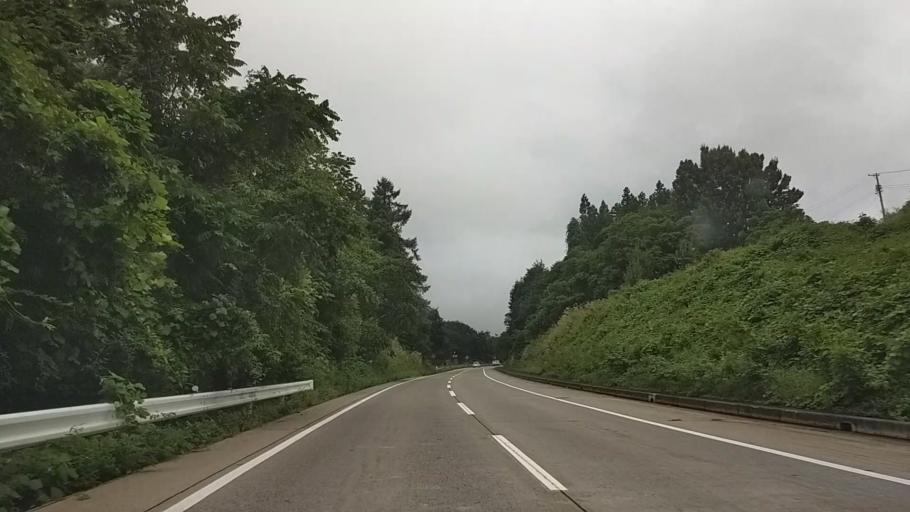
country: JP
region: Nagano
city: Iiyama
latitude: 36.8166
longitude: 138.3441
